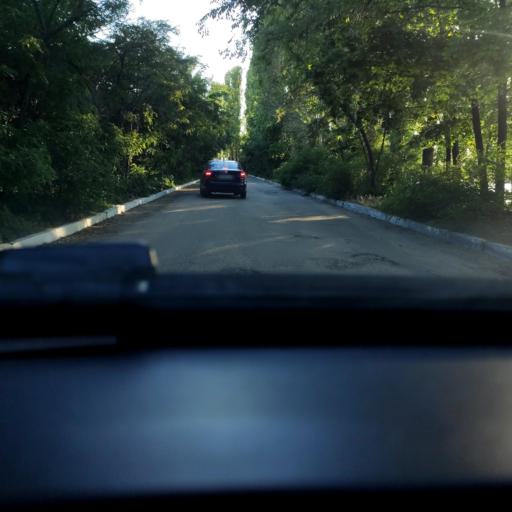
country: RU
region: Voronezj
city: Shilovo
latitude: 51.5377
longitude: 39.1413
